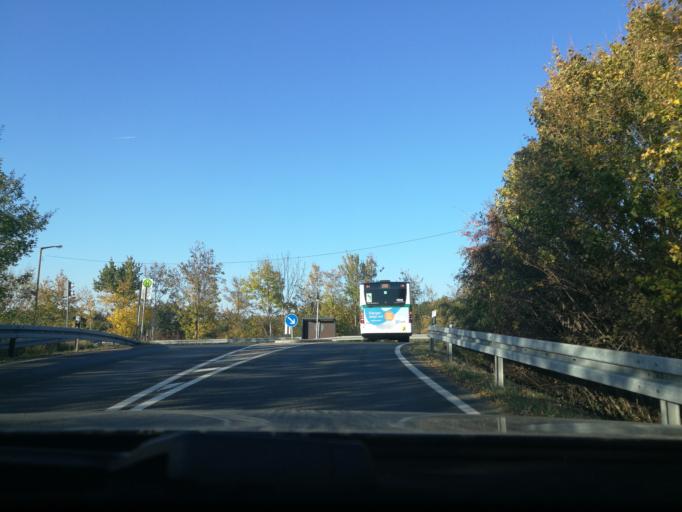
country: DE
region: Bavaria
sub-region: Regierungsbezirk Mittelfranken
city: Wetzendorf
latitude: 49.5314
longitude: 11.0322
